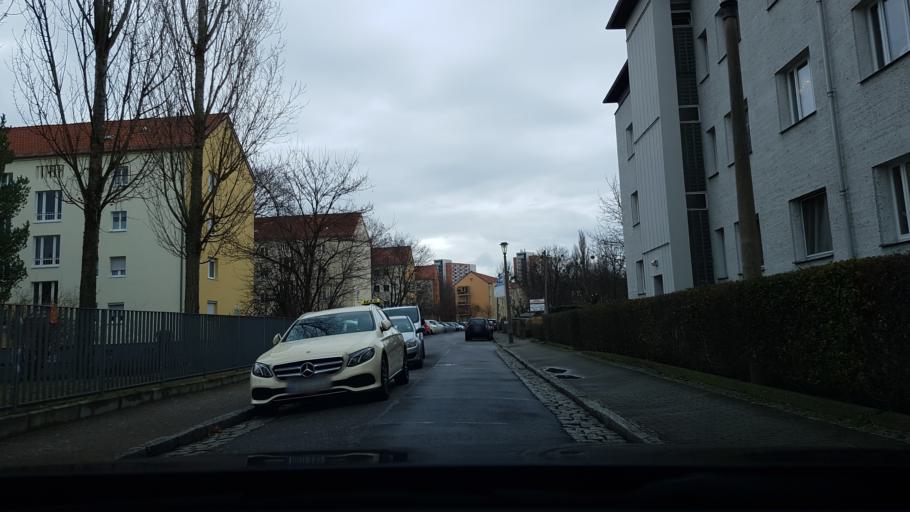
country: DE
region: Saxony
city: Dresden
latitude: 51.0113
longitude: 13.7897
